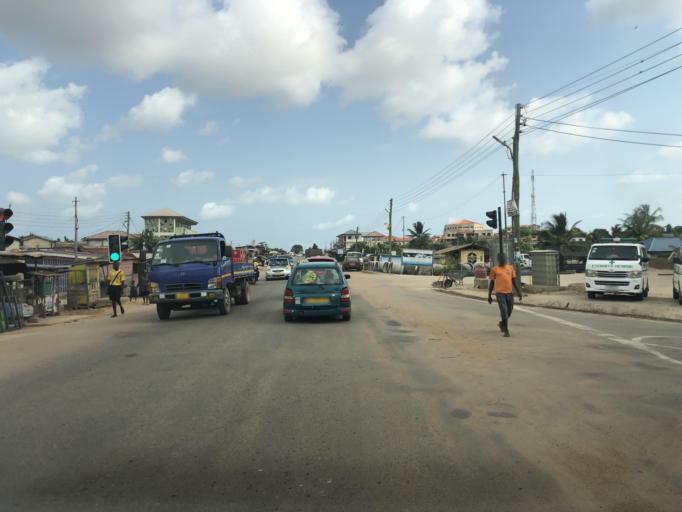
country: GH
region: Central
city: Cape Coast
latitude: 5.1441
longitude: -1.2857
